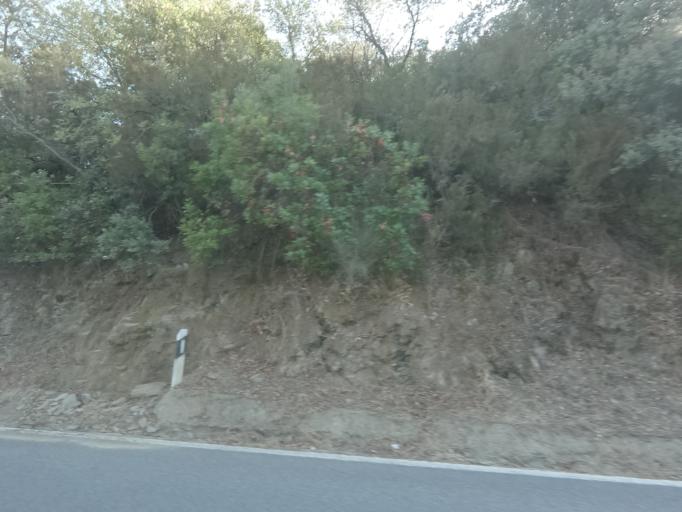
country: PT
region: Viseu
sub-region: Tabuaco
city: Tabuaco
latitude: 41.1521
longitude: -7.5821
